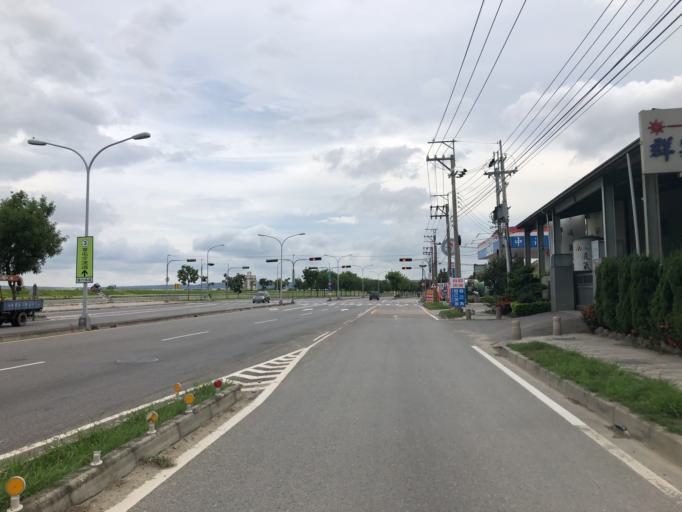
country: TW
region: Taiwan
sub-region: Taichung City
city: Taichung
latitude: 24.0863
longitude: 120.6770
